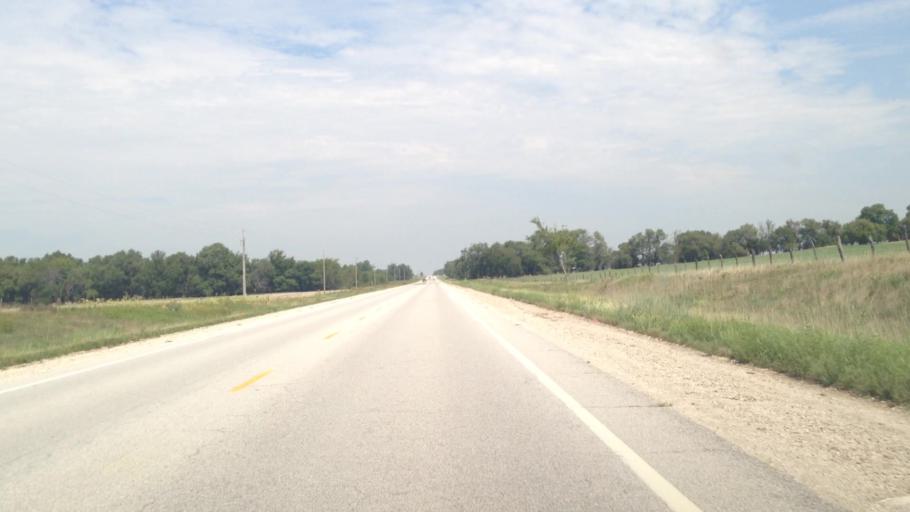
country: US
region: Kansas
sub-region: Neosho County
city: Erie
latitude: 37.4607
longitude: -95.2696
